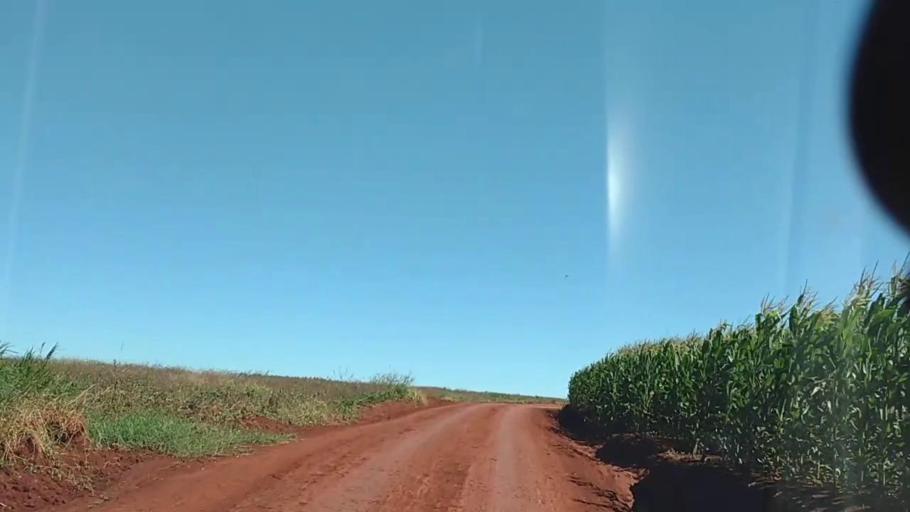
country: PY
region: Alto Parana
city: Naranjal
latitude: -25.9477
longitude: -55.1056
